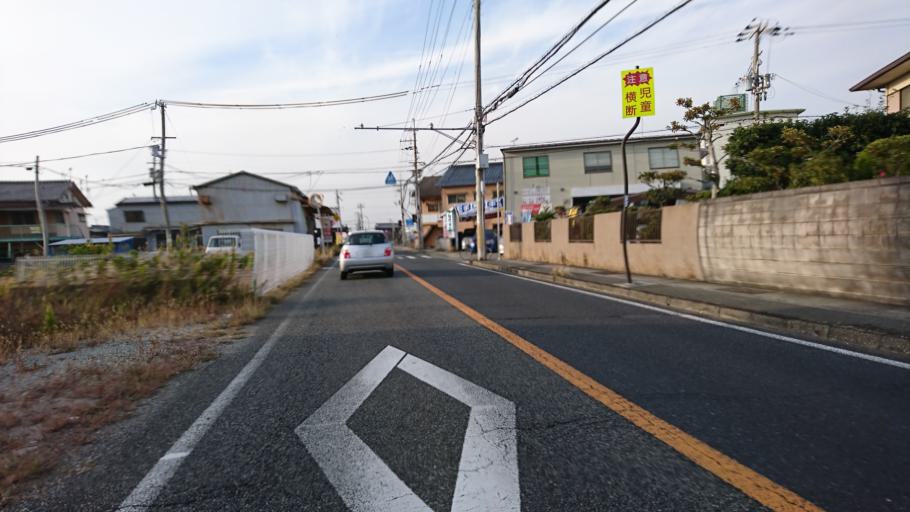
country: JP
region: Hyogo
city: Kakogawacho-honmachi
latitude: 34.7113
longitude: 134.8643
